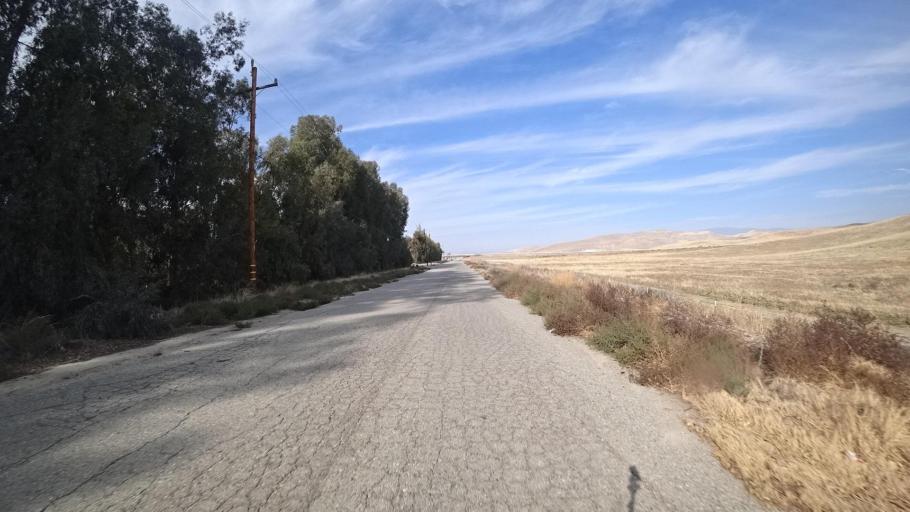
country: US
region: California
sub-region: Kern County
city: Arvin
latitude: 35.2881
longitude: -118.7527
